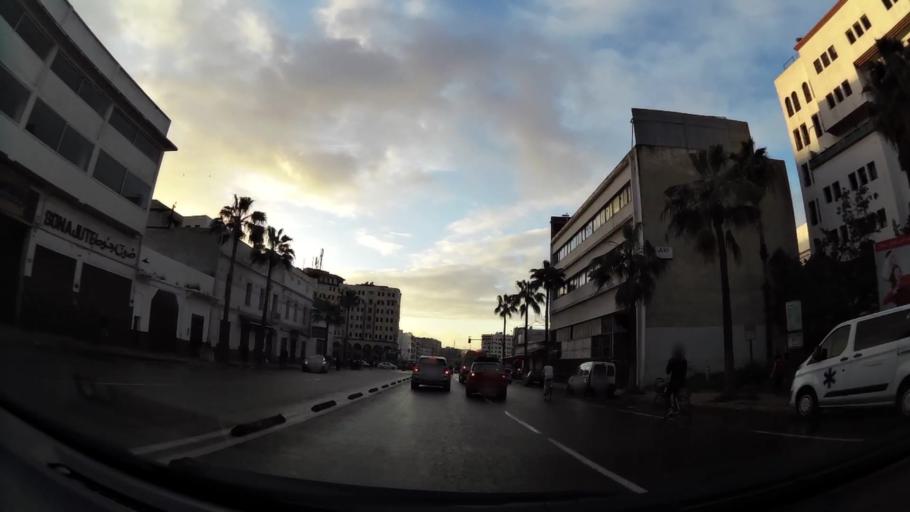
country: MA
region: Grand Casablanca
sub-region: Casablanca
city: Casablanca
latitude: 33.5847
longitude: -7.6057
